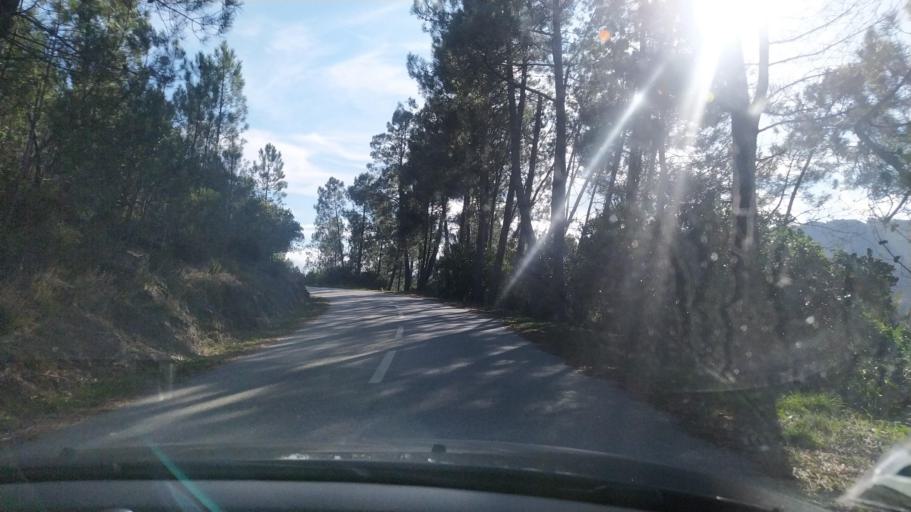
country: PT
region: Coimbra
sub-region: Oliveira do Hospital
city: Oliveira do Hospital
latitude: 40.2036
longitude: -7.7386
